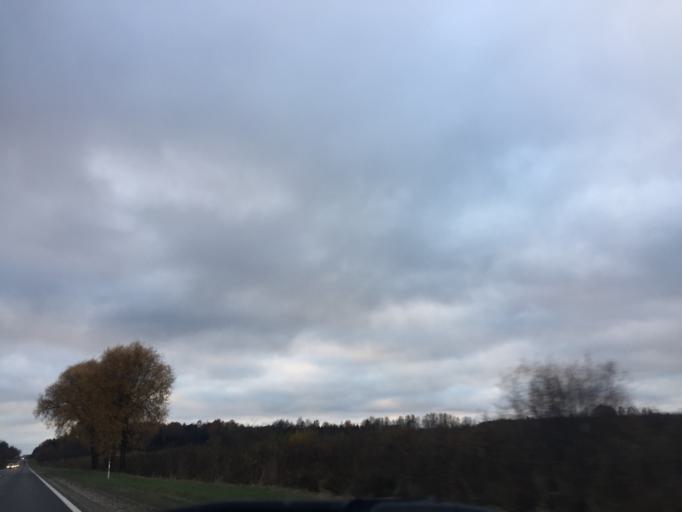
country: LV
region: Skrunda
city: Skrunda
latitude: 56.6676
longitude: 21.9756
